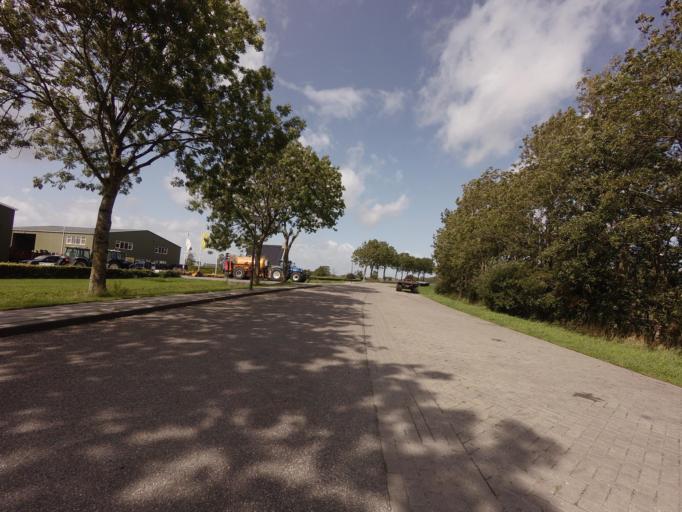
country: NL
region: Friesland
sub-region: Gemeente Harlingen
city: Harlingen
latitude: 53.1492
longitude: 5.4774
